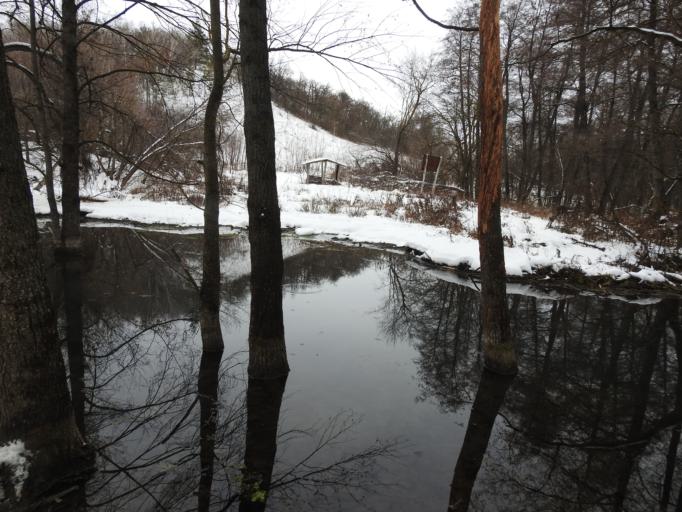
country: RU
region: Saratov
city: Tersa
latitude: 52.1082
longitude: 47.4711
